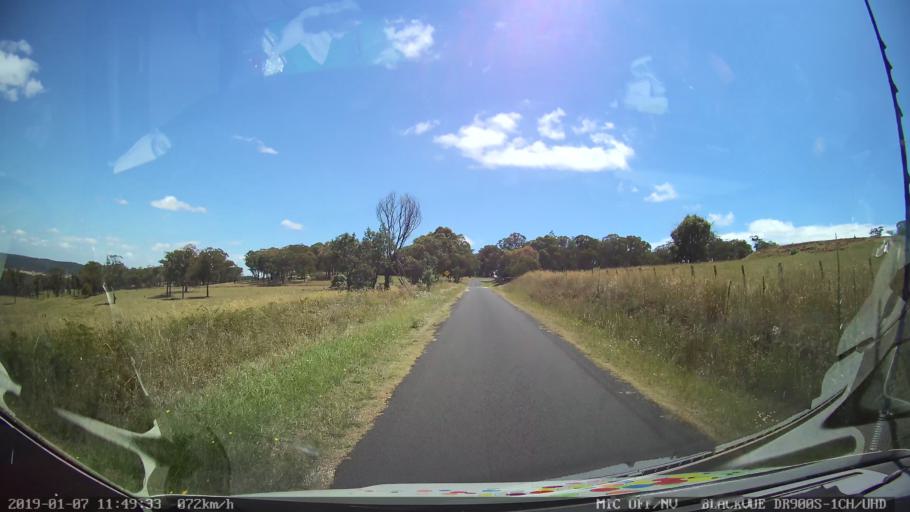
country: AU
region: New South Wales
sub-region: Guyra
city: Guyra
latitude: -30.3178
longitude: 151.6291
